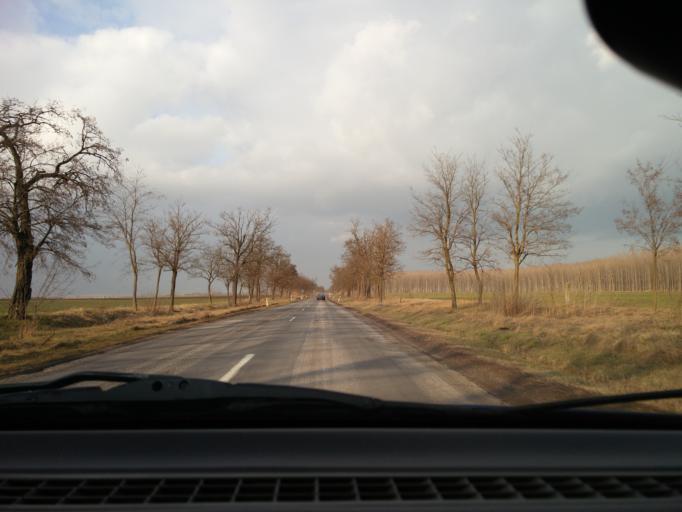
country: HU
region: Pest
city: Tapioszolos
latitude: 47.2981
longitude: 19.8690
